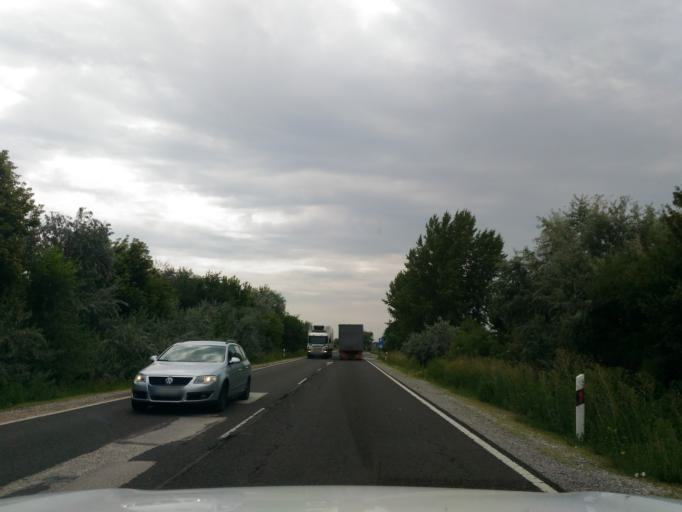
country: HU
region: Jasz-Nagykun-Szolnok
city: Toszeg
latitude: 47.1572
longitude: 20.1176
